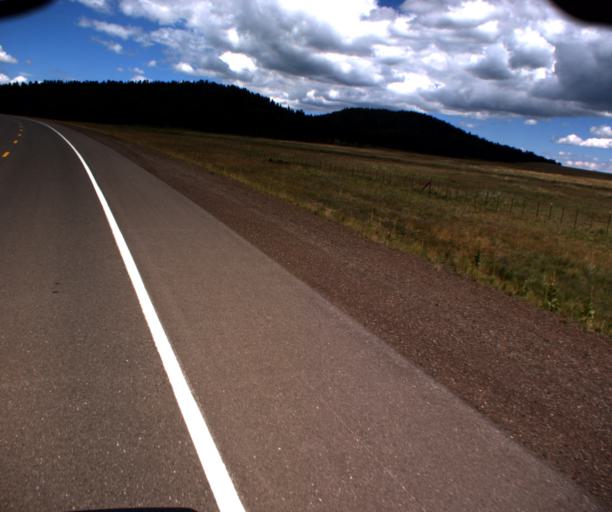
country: US
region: Arizona
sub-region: Apache County
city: Eagar
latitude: 34.0136
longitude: -109.5673
